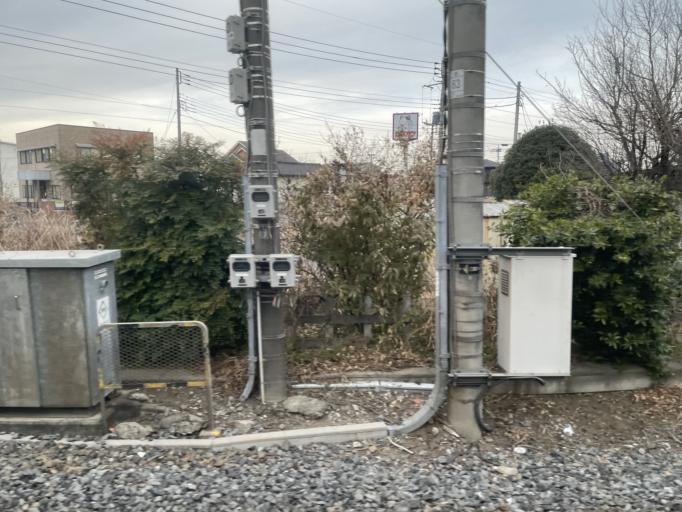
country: JP
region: Ibaraki
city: Koga
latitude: 36.1603
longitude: 139.7179
